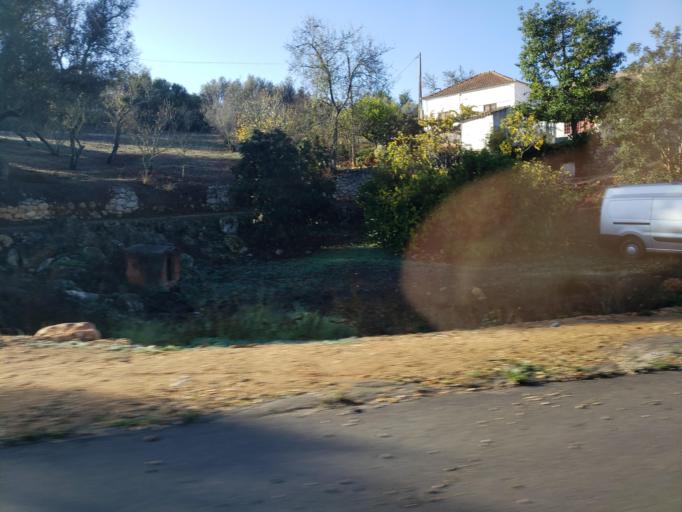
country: PT
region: Faro
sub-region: Portimao
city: Portimao
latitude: 37.1585
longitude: -8.5637
